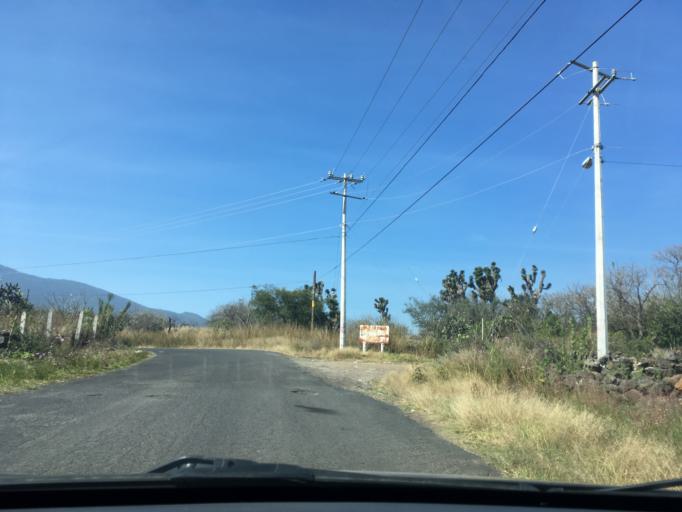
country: MX
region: Michoacan
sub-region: Morelia
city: La Mintzita (Piedra Dura)
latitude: 19.6492
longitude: -101.2993
